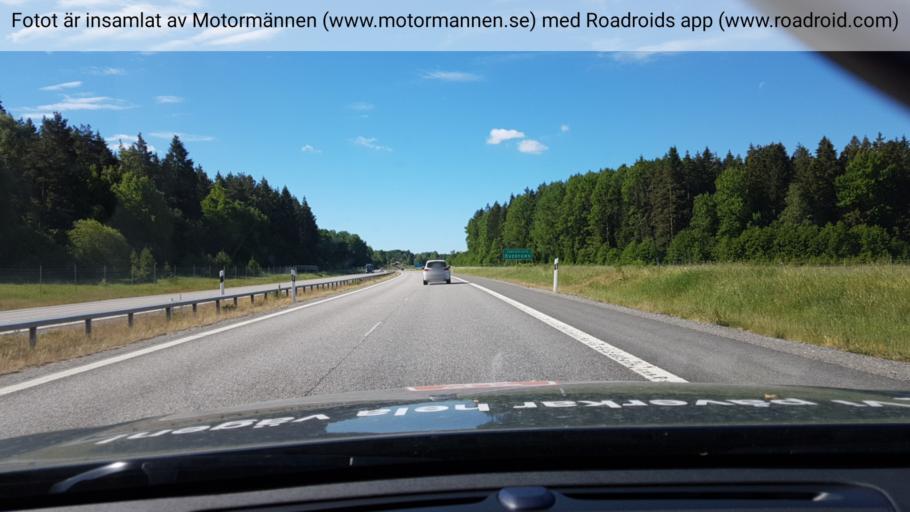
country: SE
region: Stockholm
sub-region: Nynashamns Kommun
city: Osmo
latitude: 59.0085
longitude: 17.9426
